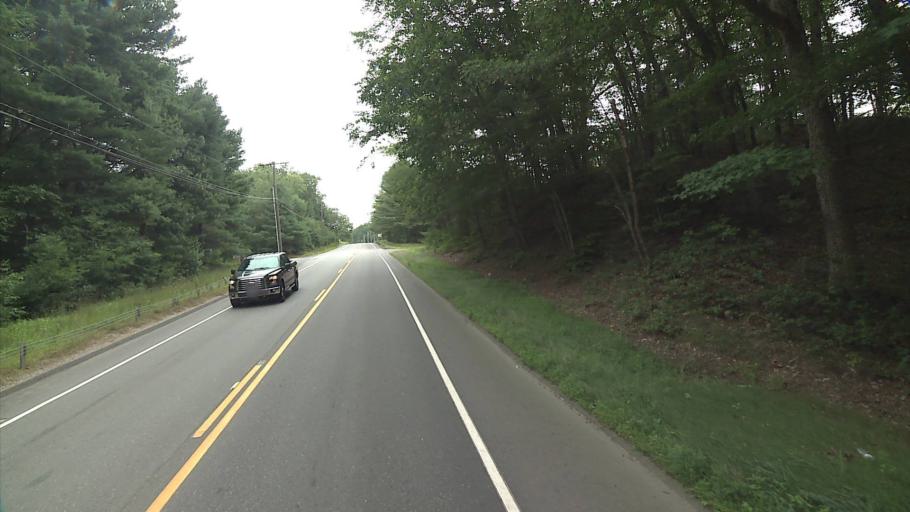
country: US
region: Connecticut
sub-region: Tolland County
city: Storrs
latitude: 41.8781
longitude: -72.2765
